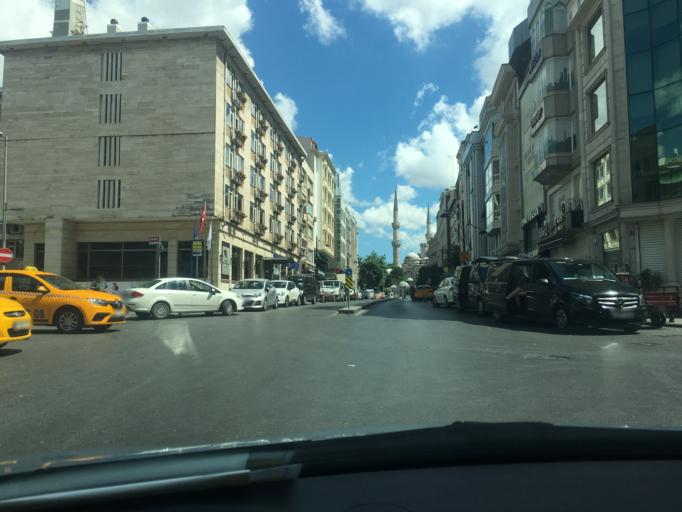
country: TR
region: Istanbul
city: Istanbul
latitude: 41.0115
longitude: 28.9554
